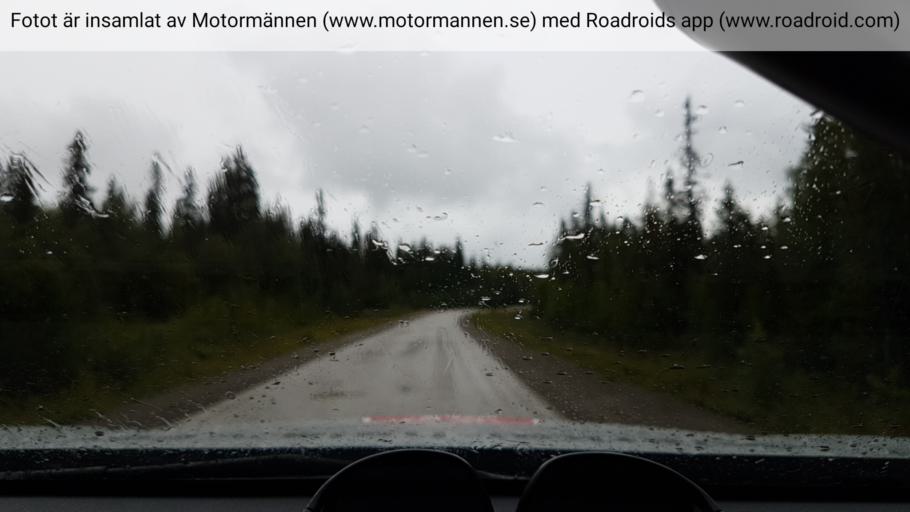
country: SE
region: Vaesterbotten
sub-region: Asele Kommun
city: Insjon
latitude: 64.8193
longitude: 17.4918
